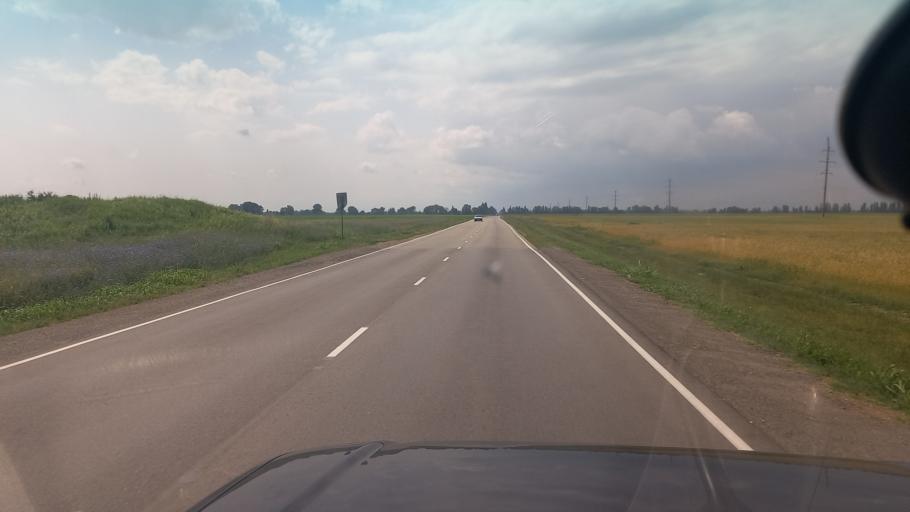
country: RU
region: Adygeya
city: Koshekhabl'
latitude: 44.9057
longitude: 40.4646
